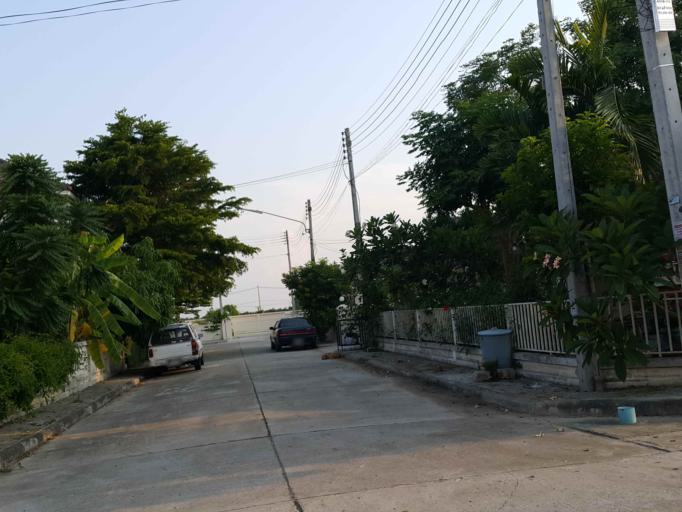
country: TH
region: Chiang Mai
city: Saraphi
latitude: 18.7126
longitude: 98.9762
